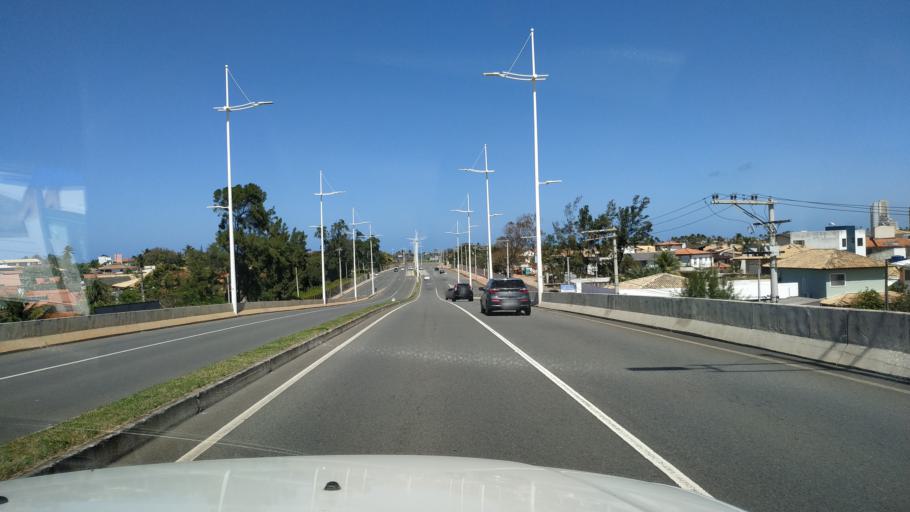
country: BR
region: Bahia
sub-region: Lauro De Freitas
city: Lauro de Freitas
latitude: -12.9490
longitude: -38.3846
